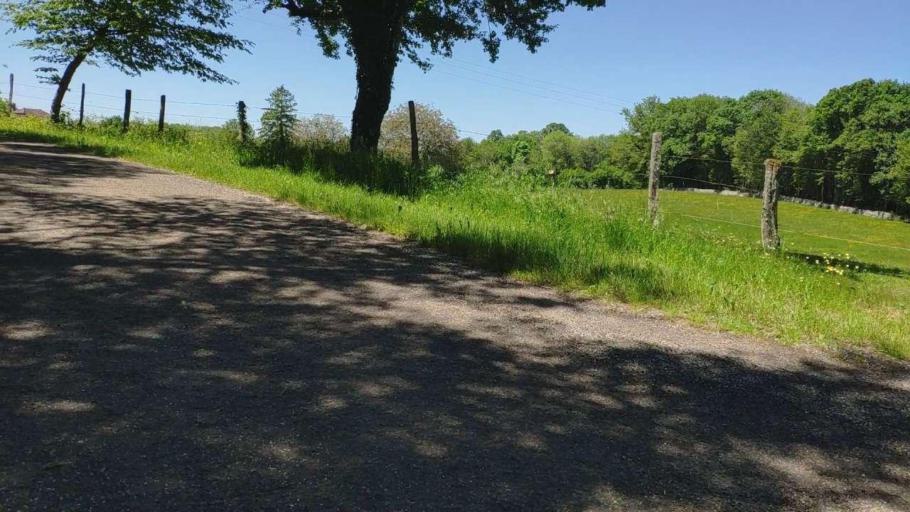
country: FR
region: Franche-Comte
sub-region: Departement du Jura
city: Poligny
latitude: 46.7431
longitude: 5.6721
